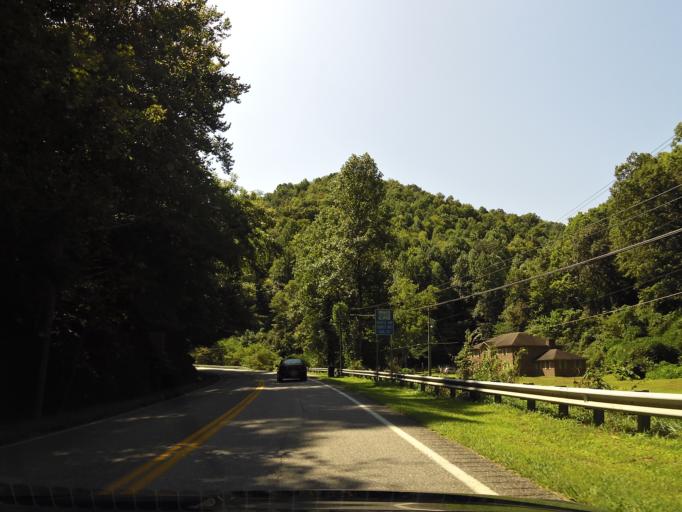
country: US
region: Kentucky
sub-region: Leslie County
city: Hyden
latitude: 37.1248
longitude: -83.3822
